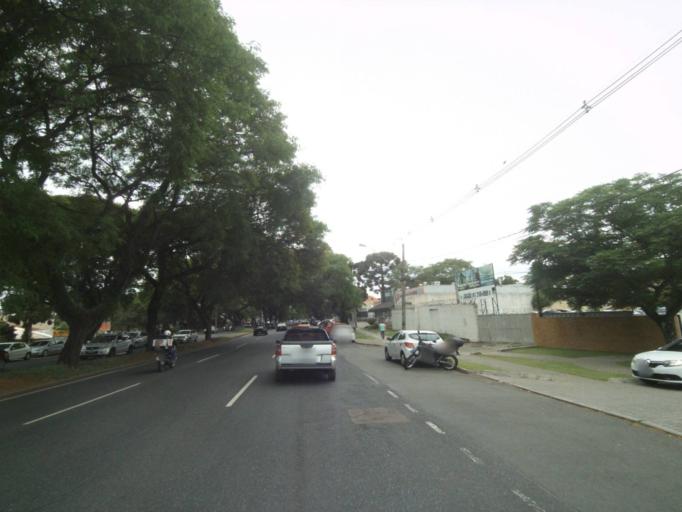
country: BR
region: Parana
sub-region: Curitiba
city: Curitiba
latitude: -25.4277
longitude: -49.2370
